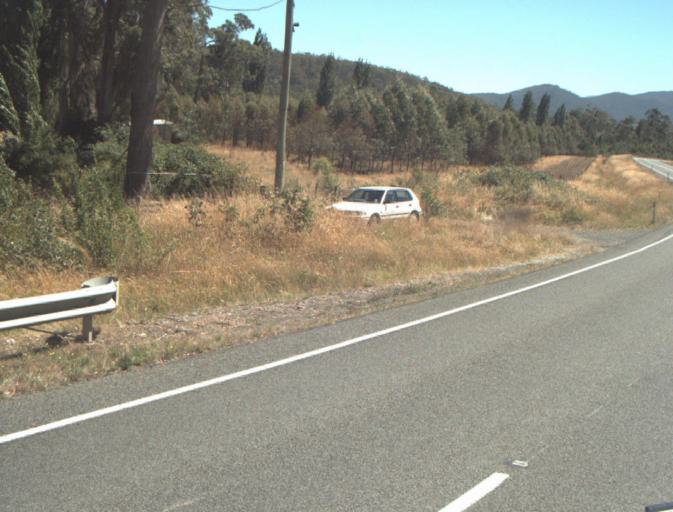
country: AU
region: Tasmania
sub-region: Launceston
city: Newstead
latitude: -41.3819
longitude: 147.3118
